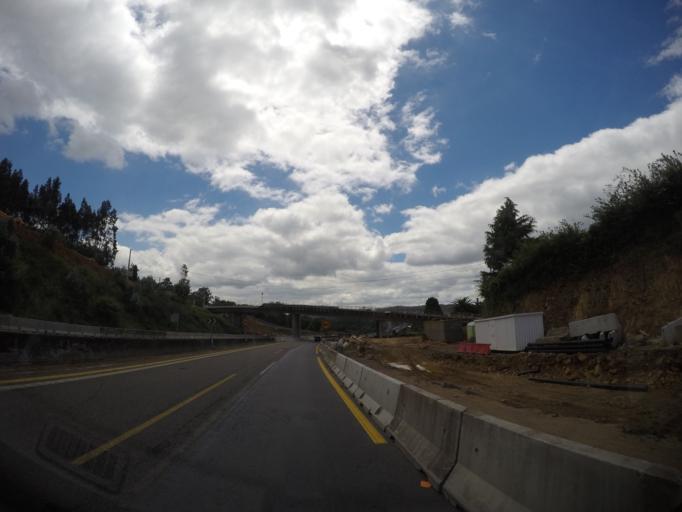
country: ES
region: Galicia
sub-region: Provincia da Coruna
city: Rois
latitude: 42.8214
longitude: -8.7526
